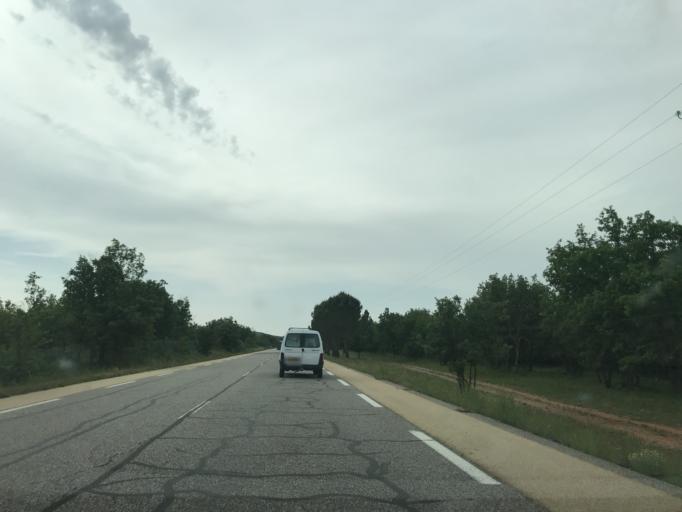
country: FR
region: Provence-Alpes-Cote d'Azur
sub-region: Departement du Var
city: Rians
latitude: 43.5585
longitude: 5.7890
